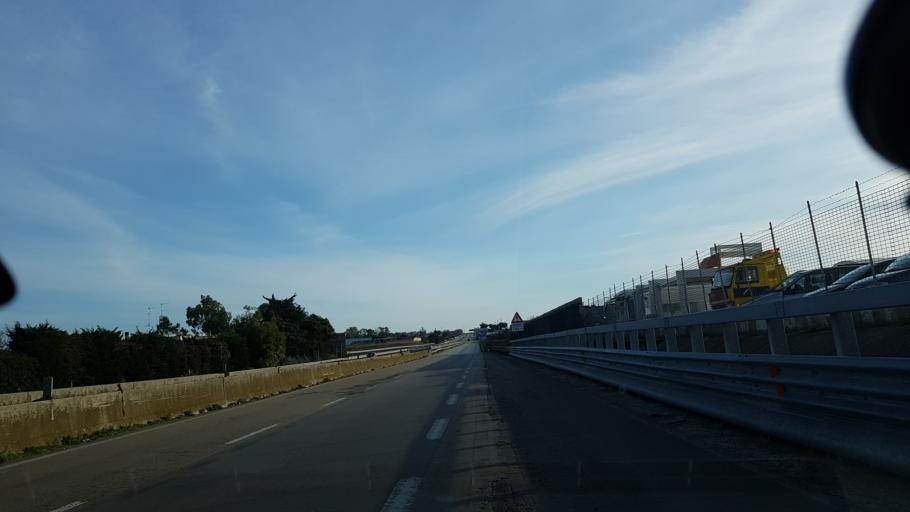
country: IT
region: Apulia
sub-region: Provincia di Brindisi
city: Brindisi
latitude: 40.6406
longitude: 17.9148
